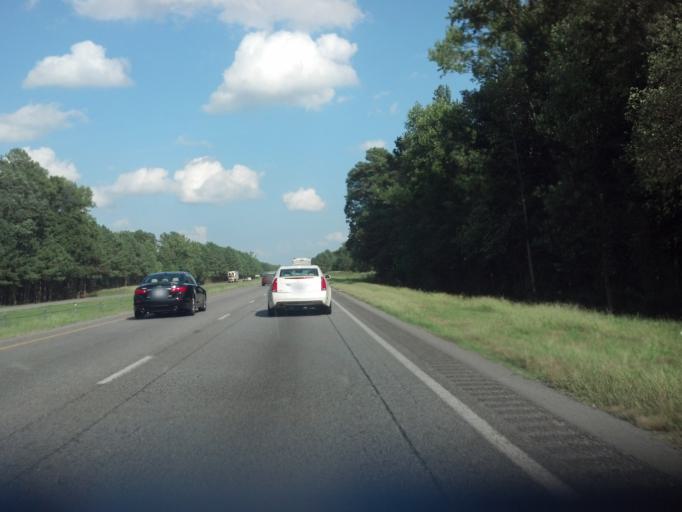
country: US
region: North Carolina
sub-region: Nash County
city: Rocky Mount
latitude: 35.9359
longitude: -77.7405
